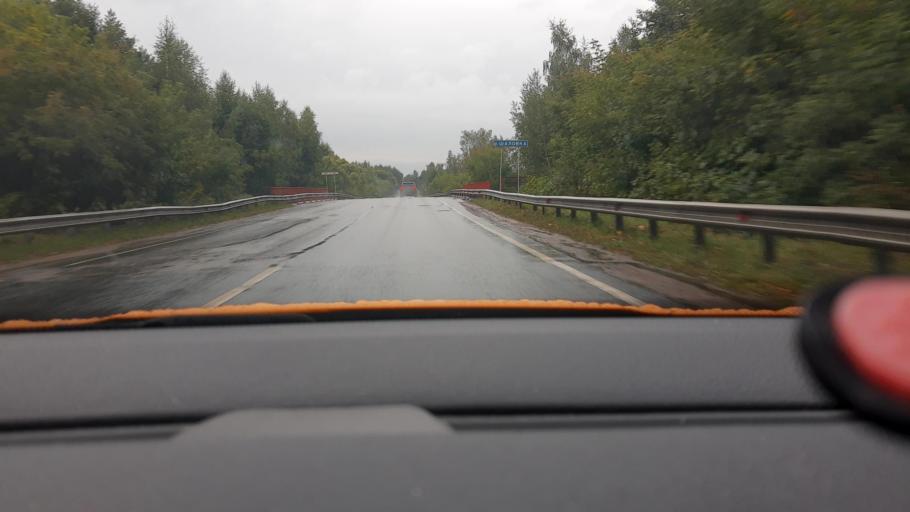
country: RU
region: Moskovskaya
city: Obukhovo
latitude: 55.8096
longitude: 38.2526
